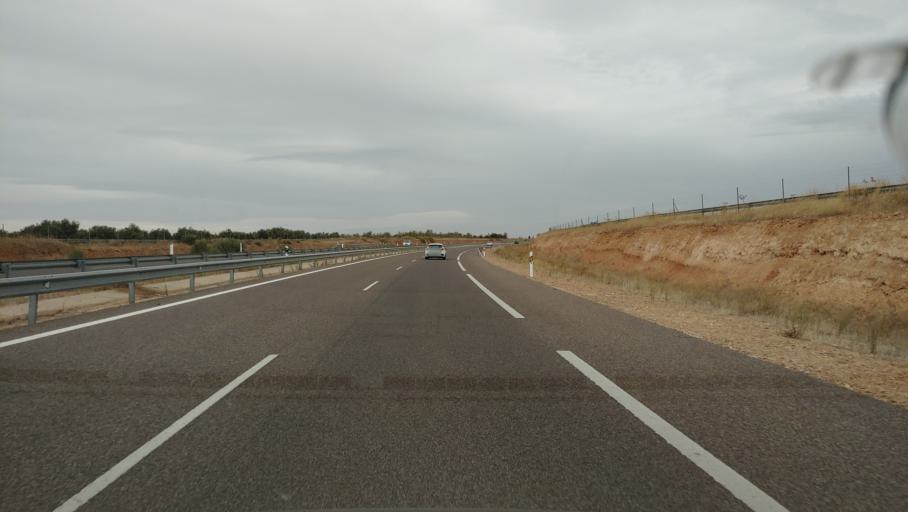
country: ES
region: Castille-La Mancha
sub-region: Provincia de Ciudad Real
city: Valenzuela de Calatrava
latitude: 38.8971
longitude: -3.8299
